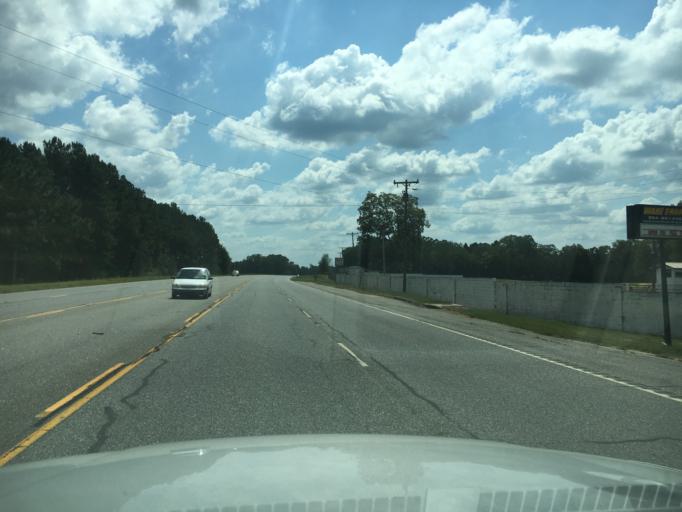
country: US
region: South Carolina
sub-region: Greenwood County
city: Ware Shoals
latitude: 34.4563
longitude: -82.2517
